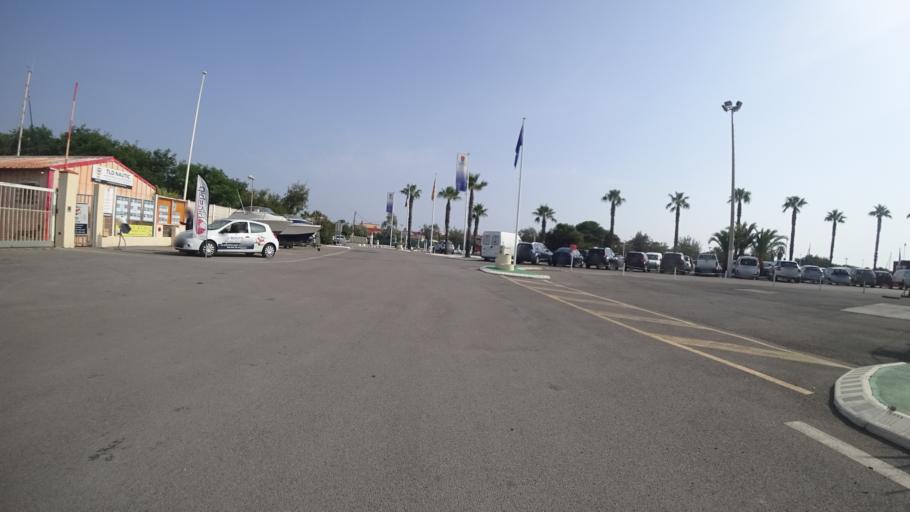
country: FR
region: Languedoc-Roussillon
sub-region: Departement des Pyrenees-Orientales
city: Sainte-Marie-Plage
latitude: 42.7230
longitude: 3.0367
